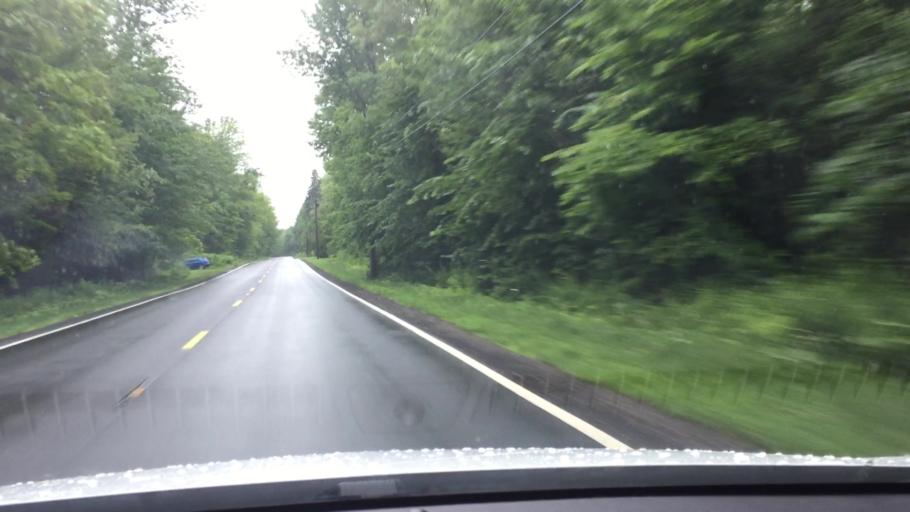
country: US
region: Massachusetts
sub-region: Berkshire County
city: Becket
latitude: 42.3531
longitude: -73.1281
